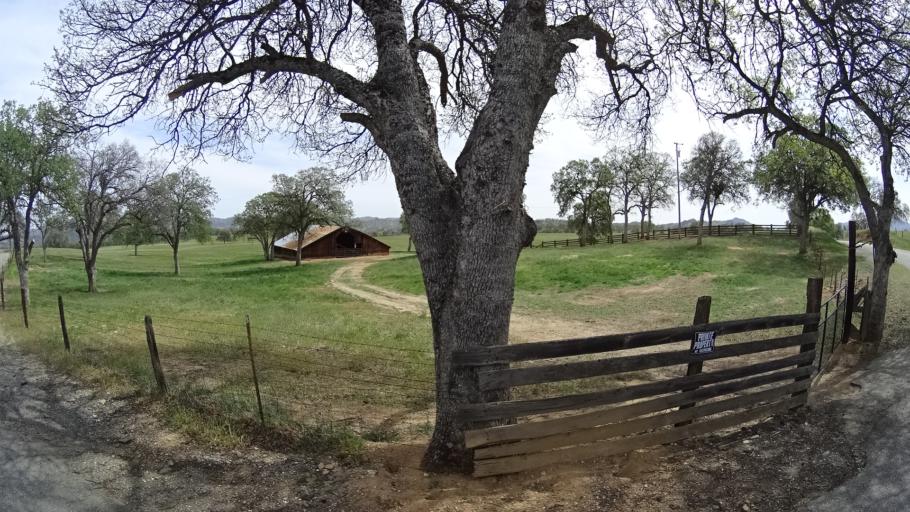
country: US
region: California
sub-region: Glenn County
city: Willows
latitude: 39.5892
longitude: -122.5773
